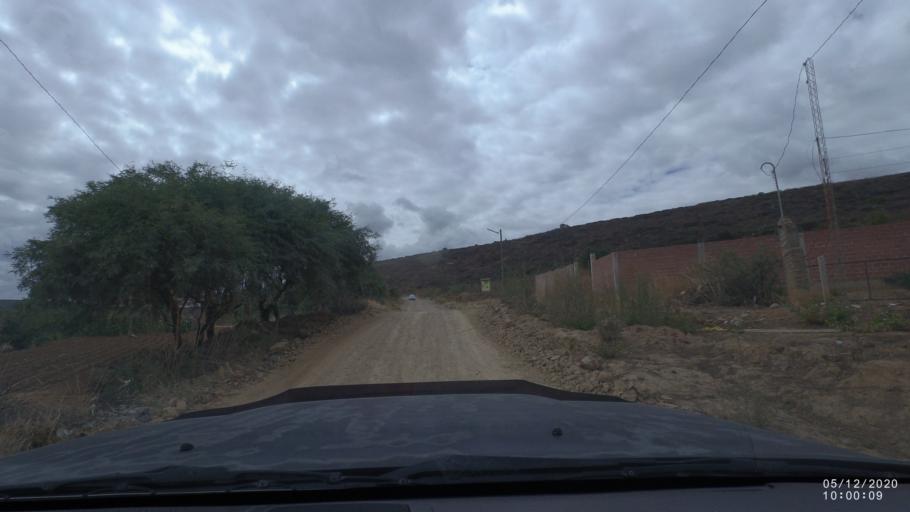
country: BO
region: Cochabamba
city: Sipe Sipe
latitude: -17.4361
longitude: -66.2902
